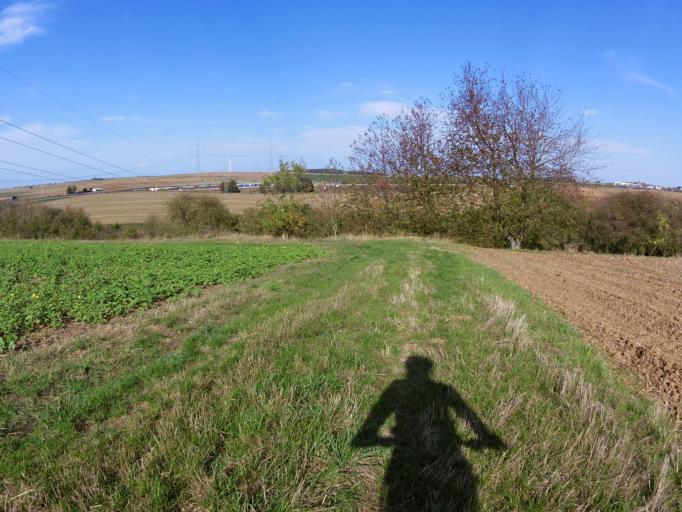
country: DE
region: Bavaria
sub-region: Regierungsbezirk Unterfranken
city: Biebelried
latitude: 49.7566
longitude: 10.0628
